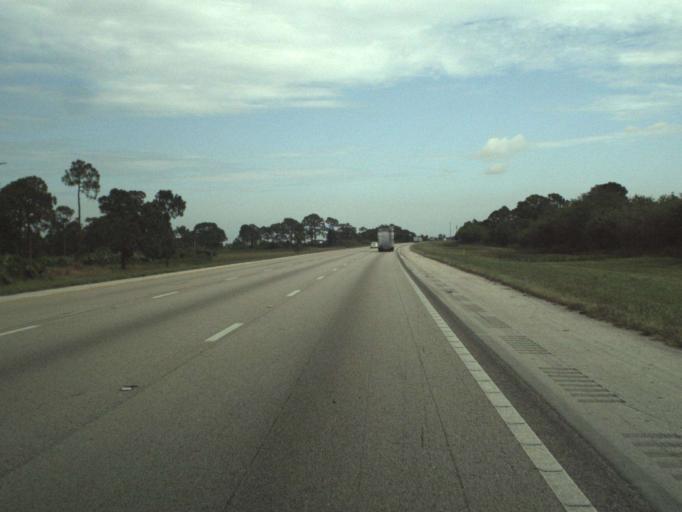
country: US
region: Florida
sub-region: Saint Lucie County
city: Port Saint Lucie
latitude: 27.1786
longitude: -80.3961
